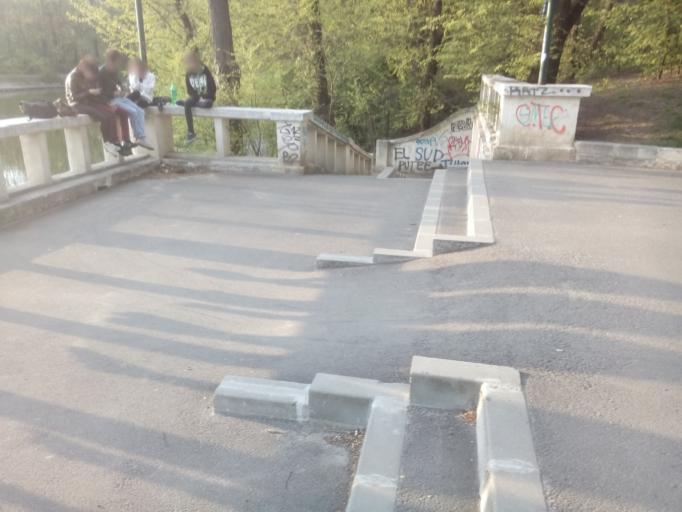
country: RO
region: Ilfov
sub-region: Comuna Fundeni-Dobroesti
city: Fundeni
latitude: 44.4345
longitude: 26.1460
